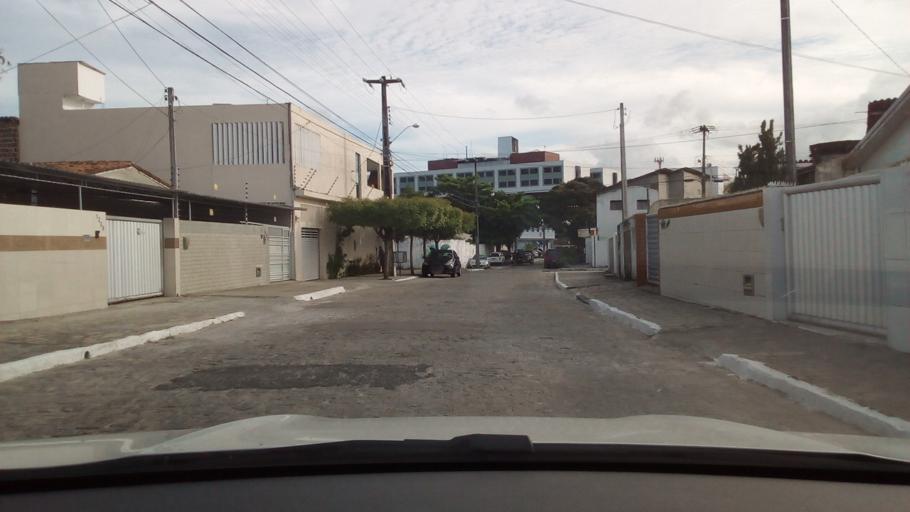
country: BR
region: Paraiba
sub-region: Joao Pessoa
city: Joao Pessoa
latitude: -7.1276
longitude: -34.8576
